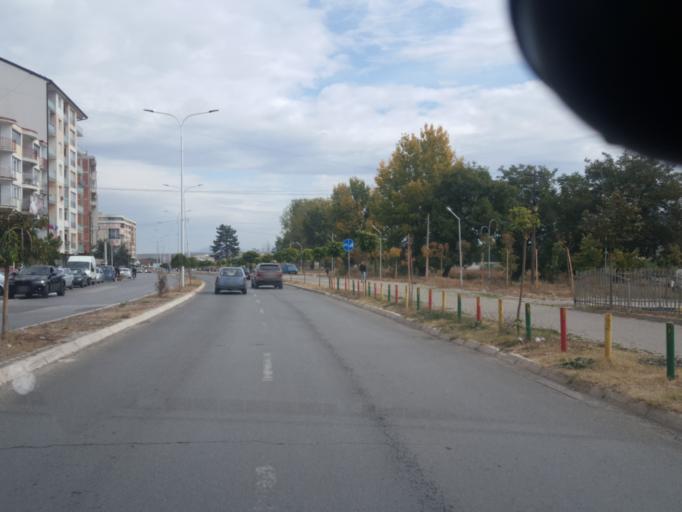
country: XK
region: Gjakova
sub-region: Komuna e Gjakoves
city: Gjakove
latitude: 42.3852
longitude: 20.4308
